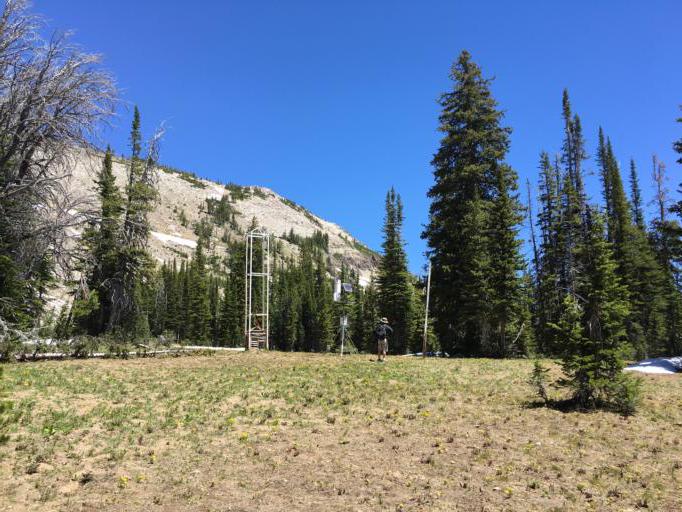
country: US
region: Wyoming
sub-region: Teton County
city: Moose Wilson Road
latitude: 43.5908
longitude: -110.8729
